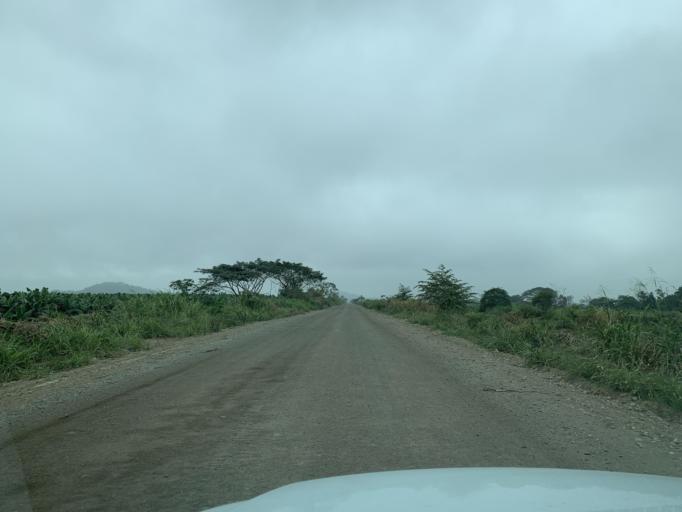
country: EC
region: Guayas
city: Coronel Marcelino Mariduena
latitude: -2.3598
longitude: -79.5792
